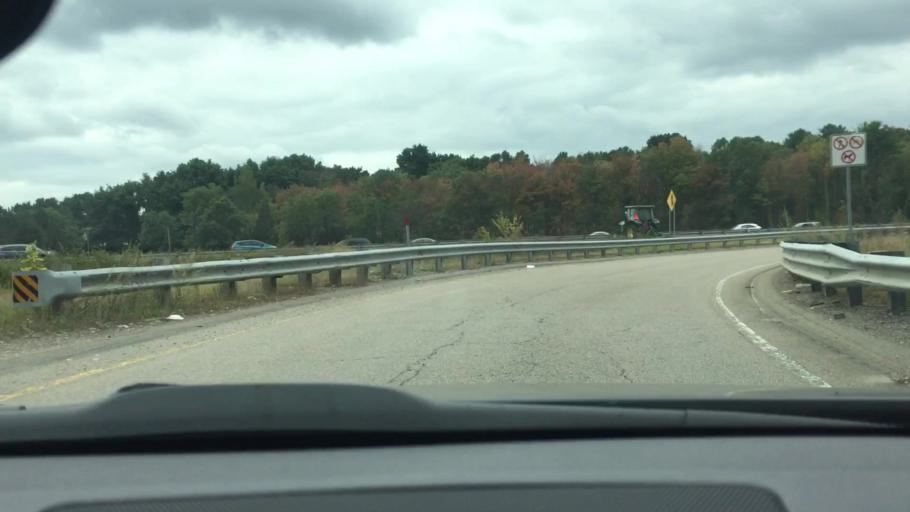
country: US
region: Massachusetts
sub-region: Norfolk County
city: Dedham
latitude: 42.2145
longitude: -71.1506
